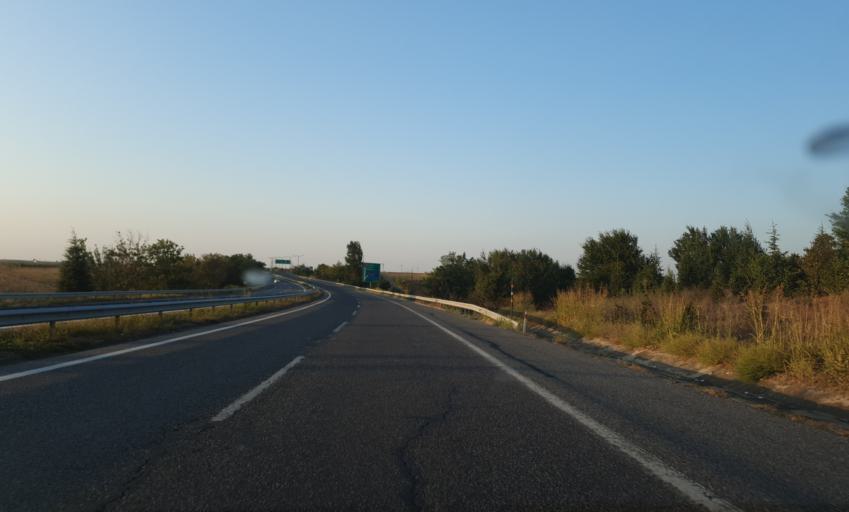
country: TR
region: Kirklareli
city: Luleburgaz
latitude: 41.4309
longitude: 27.3851
